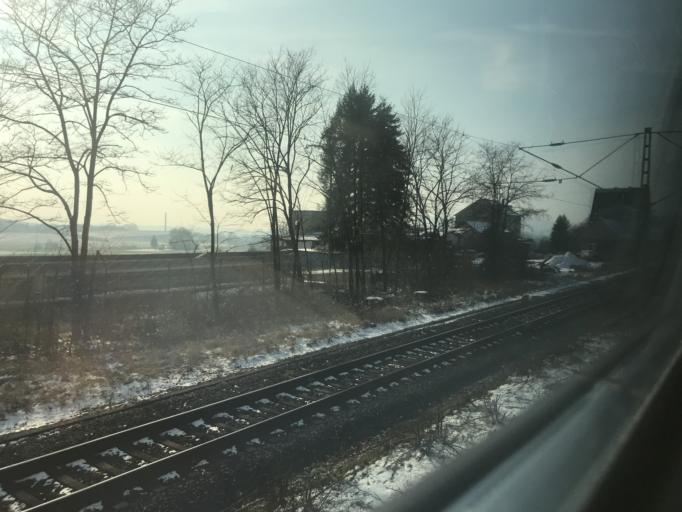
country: DE
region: Rheinland-Pfalz
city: Salmtal
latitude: 49.9297
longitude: 6.8621
